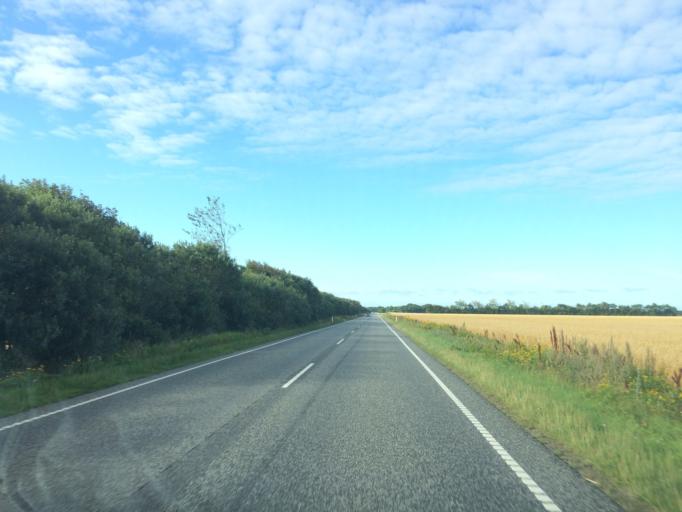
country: DK
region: Central Jutland
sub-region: Ringkobing-Skjern Kommune
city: Skjern
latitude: 55.8639
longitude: 8.3857
